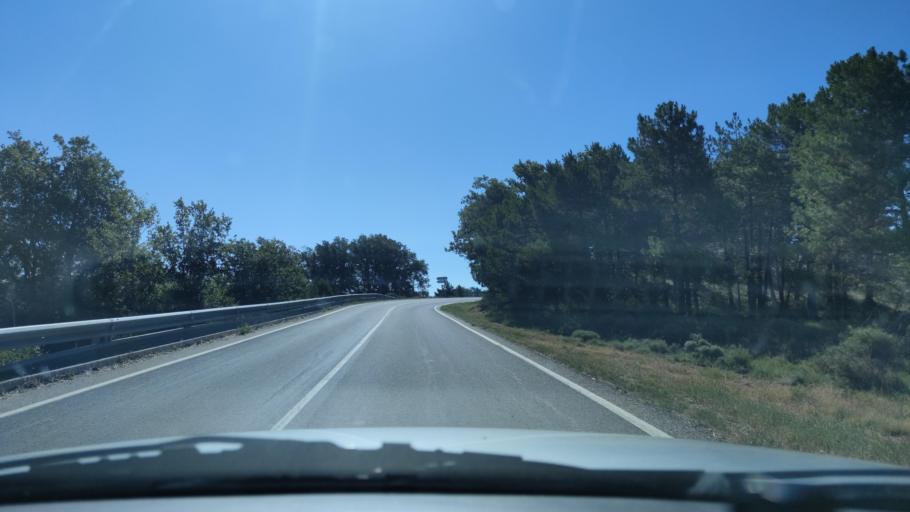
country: ES
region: Catalonia
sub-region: Provincia de Lleida
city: Solsona
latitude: 41.9186
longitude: 1.5002
